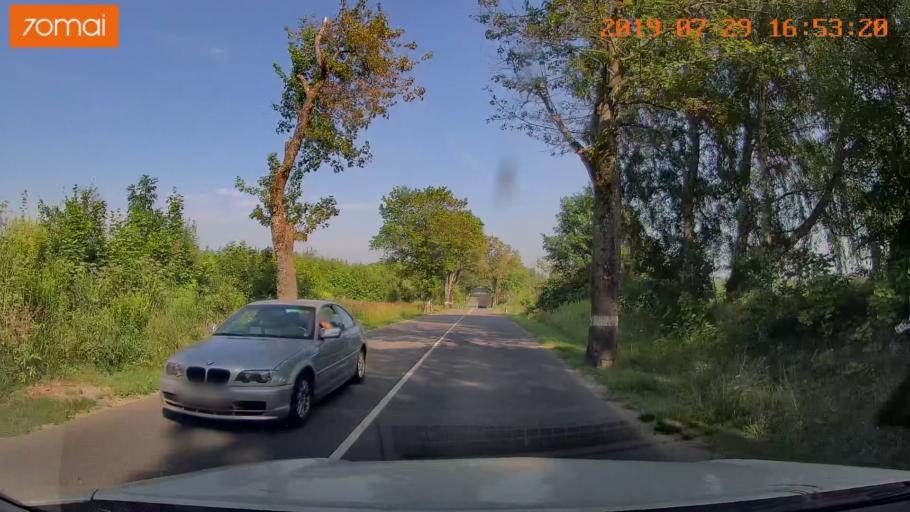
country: RU
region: Kaliningrad
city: Primorsk
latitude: 54.8134
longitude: 20.1070
